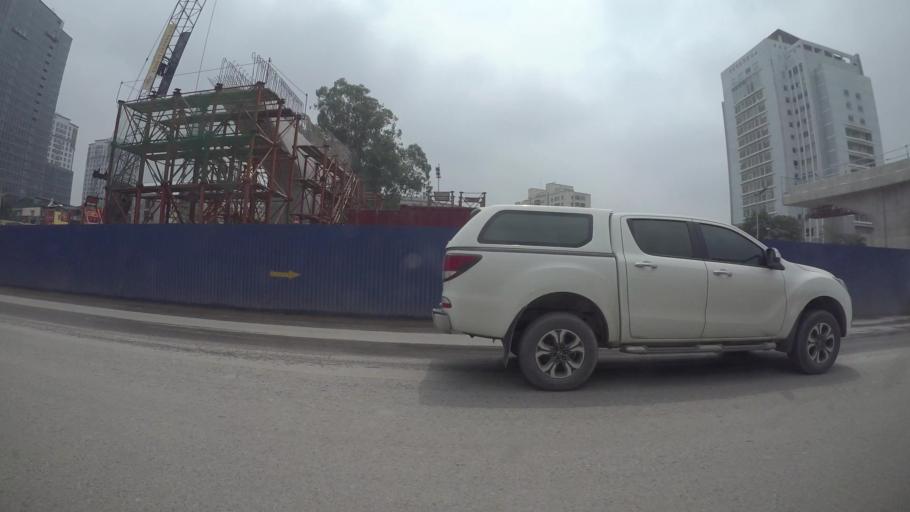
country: VN
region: Ha Noi
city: Cau Dien
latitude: 21.0483
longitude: 105.7813
